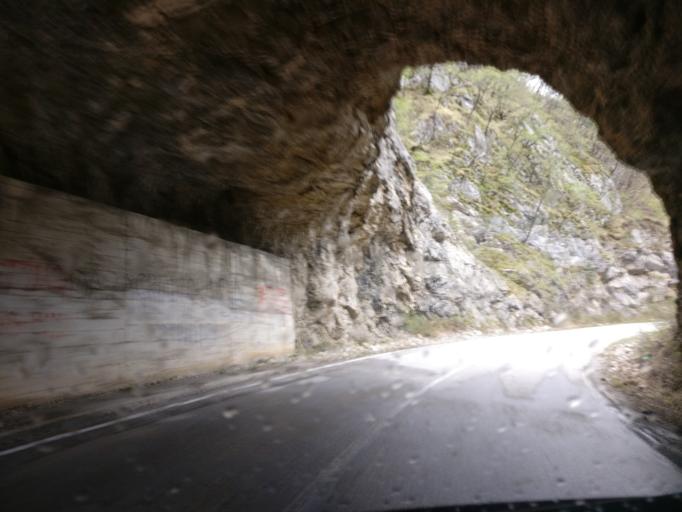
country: ME
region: Opstina Pluzine
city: Pluzine
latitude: 43.2277
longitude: 18.8477
